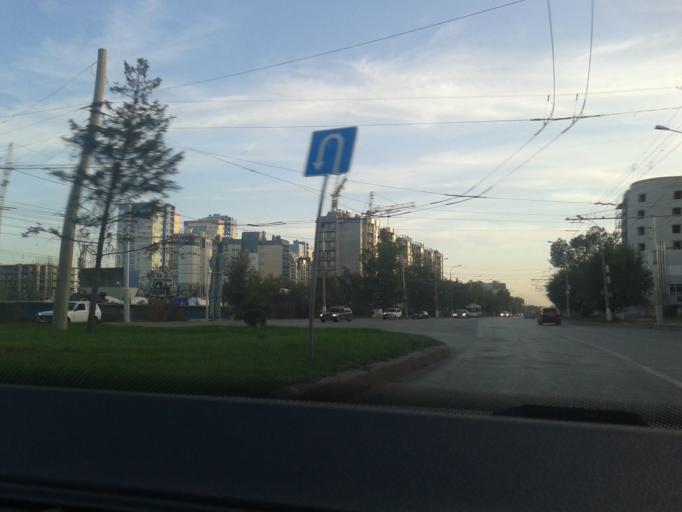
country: RU
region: Volgograd
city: Krasnoslobodsk
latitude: 48.7355
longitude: 44.5437
